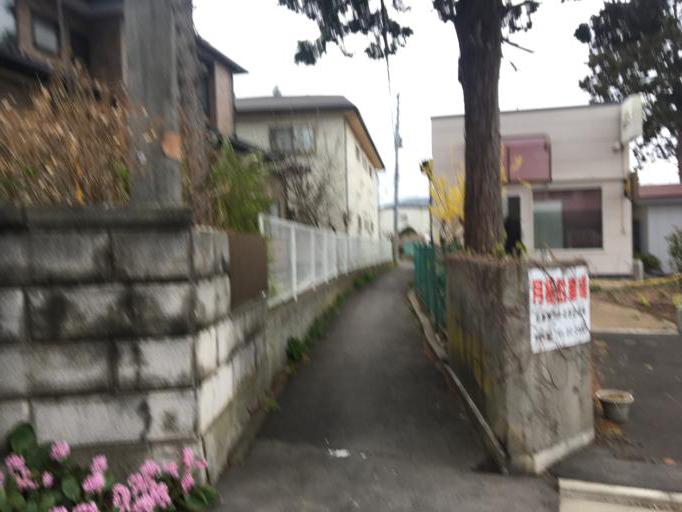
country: JP
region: Aomori
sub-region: Hachinohe Shi
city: Uchimaru
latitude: 40.5194
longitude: 141.5188
